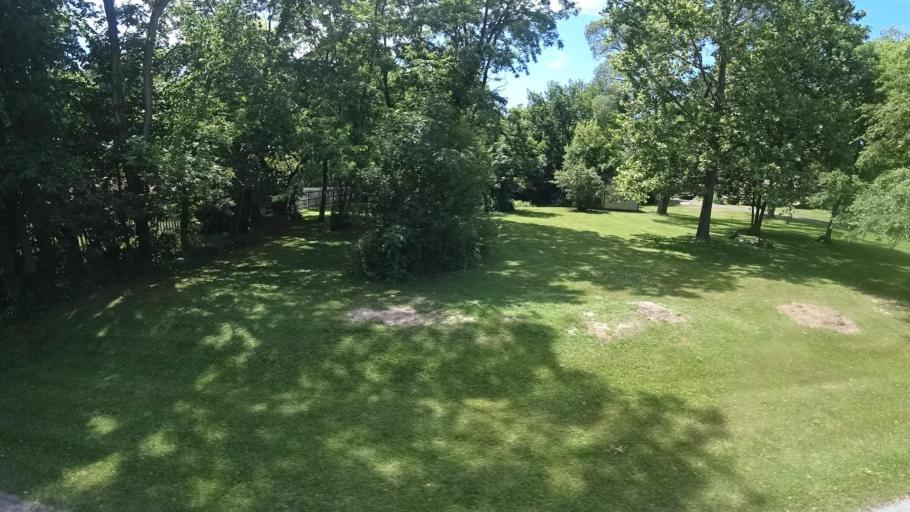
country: US
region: Indiana
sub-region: Porter County
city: Porter
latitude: 41.6303
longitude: -87.0771
